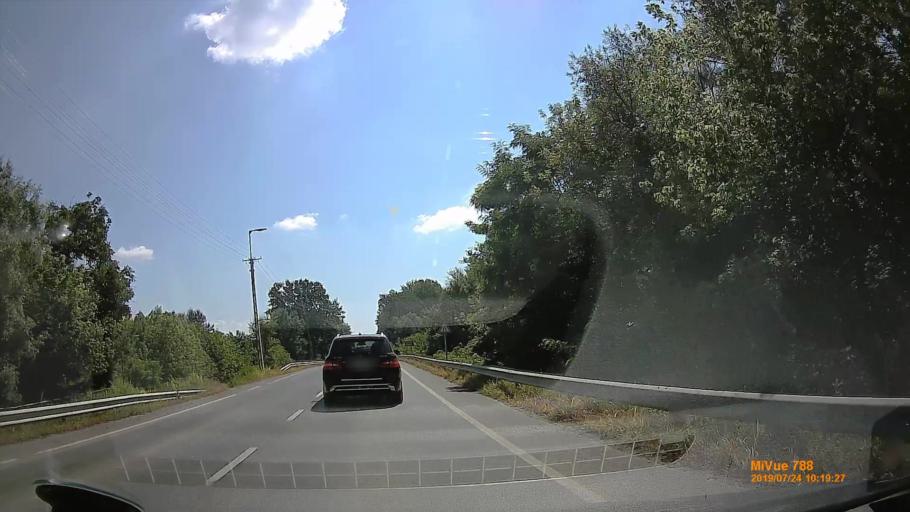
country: HU
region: Szabolcs-Szatmar-Bereg
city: Vasarosnameny
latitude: 48.1270
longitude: 22.3273
